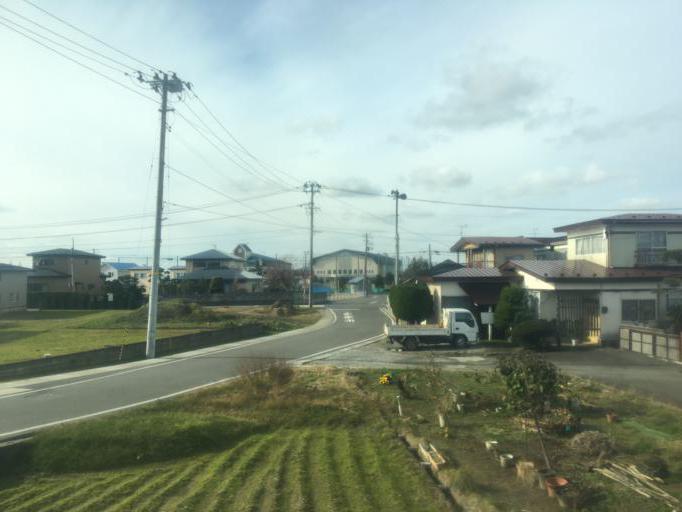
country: JP
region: Akita
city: Tenno
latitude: 39.9541
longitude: 140.0769
